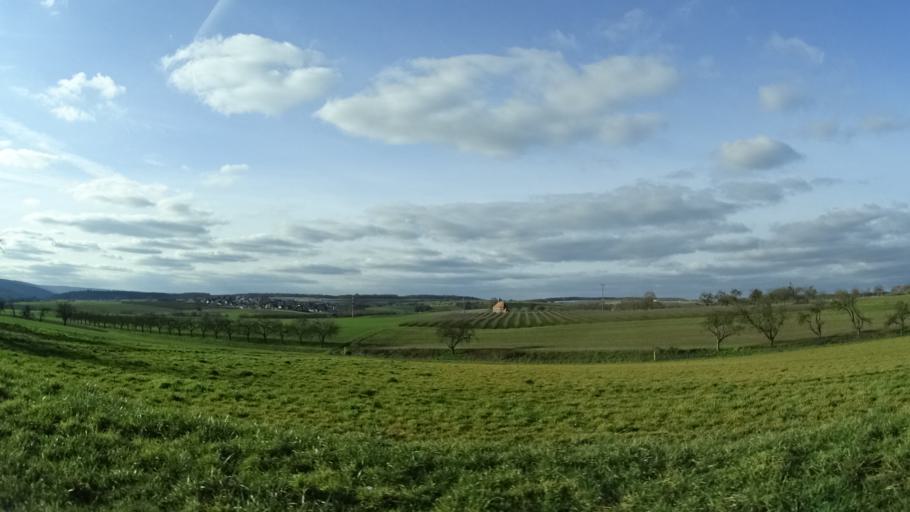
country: DE
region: Bavaria
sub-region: Regierungsbezirk Unterfranken
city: Monchberg
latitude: 49.7856
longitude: 9.2593
